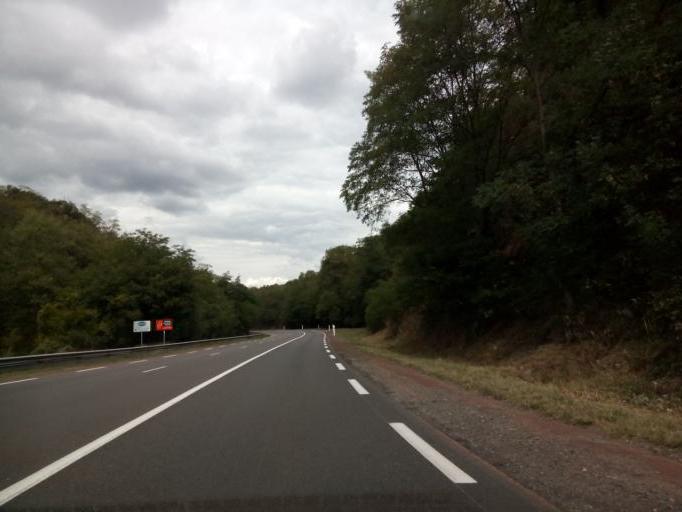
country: FR
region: Rhone-Alpes
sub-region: Departement du Rhone
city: Lissieu
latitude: 45.8479
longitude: 4.7185
